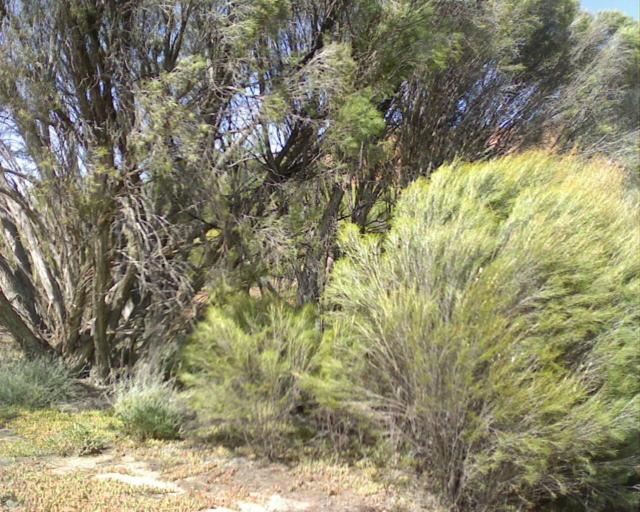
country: AU
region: Western Australia
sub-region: Merredin
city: Merredin
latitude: -30.9528
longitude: 118.8819
